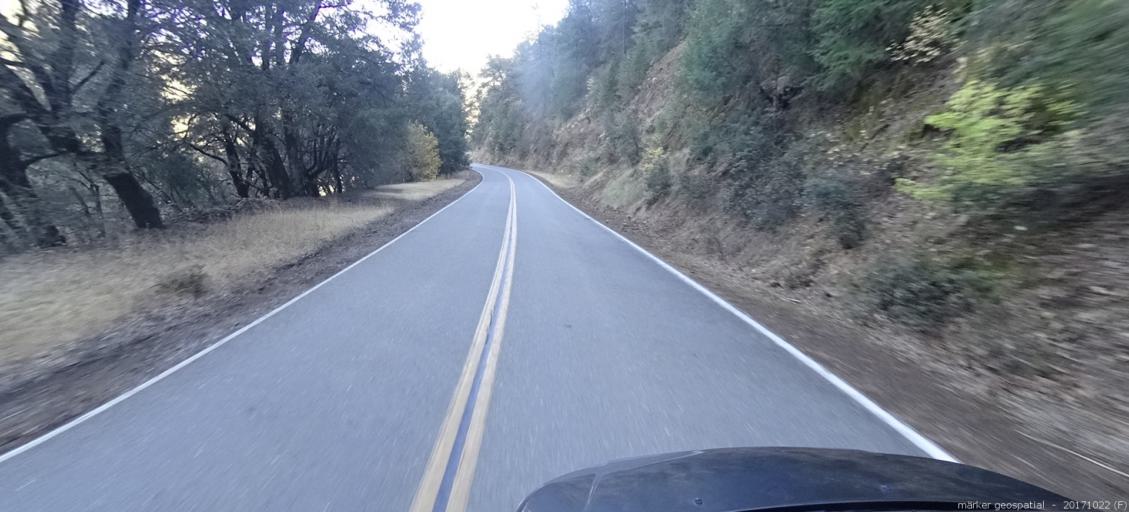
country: US
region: California
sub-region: Shasta County
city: Bella Vista
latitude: 40.9012
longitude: -122.2320
